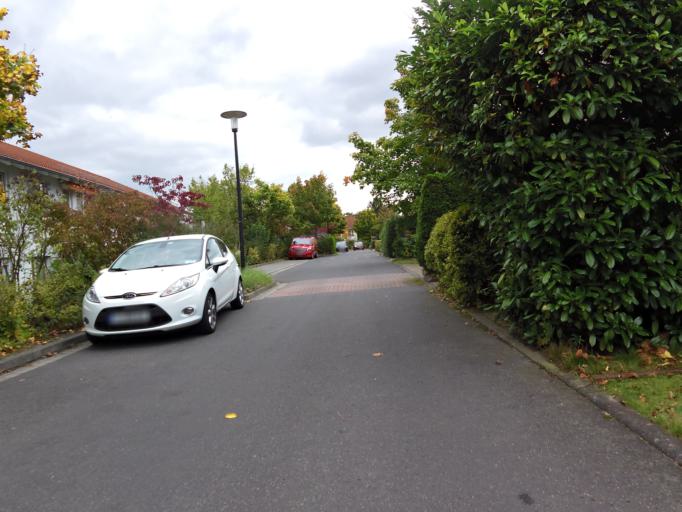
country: DE
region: Saxony
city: Grossposna
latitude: 51.3120
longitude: 12.4550
